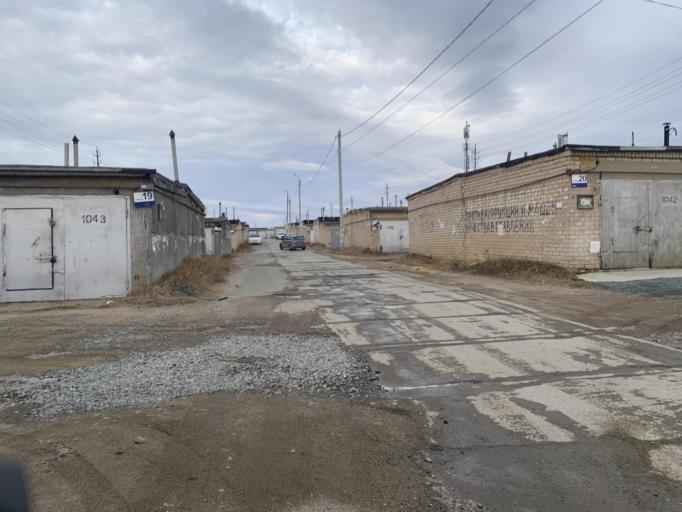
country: RU
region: Chelyabinsk
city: Roshchino
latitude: 55.1866
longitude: 61.2674
